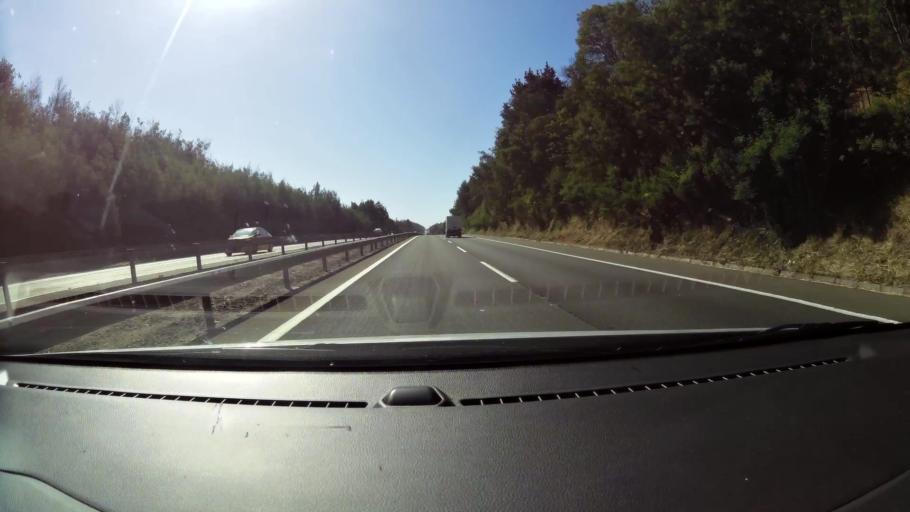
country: CL
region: Valparaiso
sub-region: Provincia de Marga Marga
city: Quilpue
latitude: -33.1770
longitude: -71.5110
